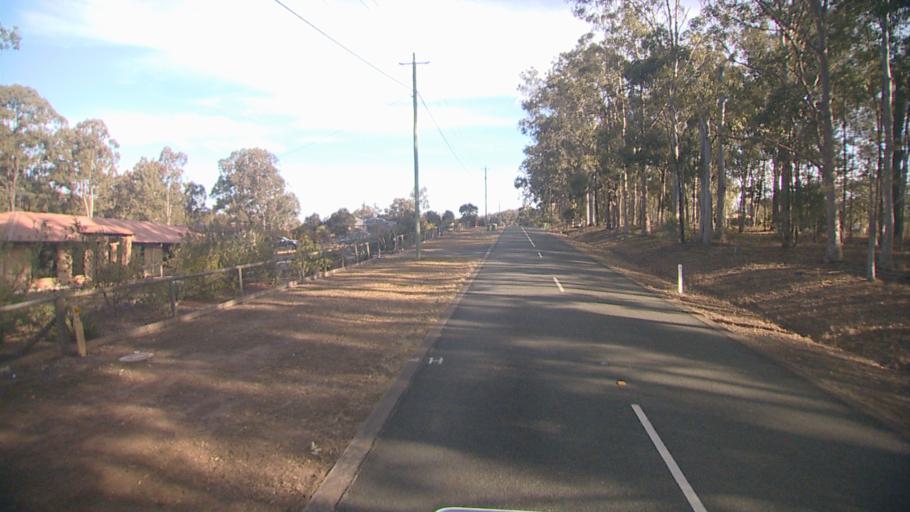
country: AU
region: Queensland
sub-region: Logan
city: Cedar Vale
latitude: -27.8826
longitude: 153.0102
